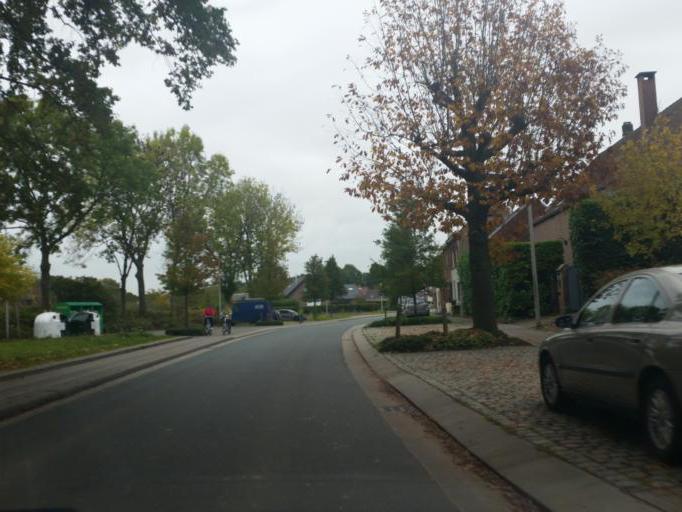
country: BE
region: Flanders
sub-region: Provincie Vlaams-Brabant
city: Beersel
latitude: 50.7560
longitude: 4.2889
